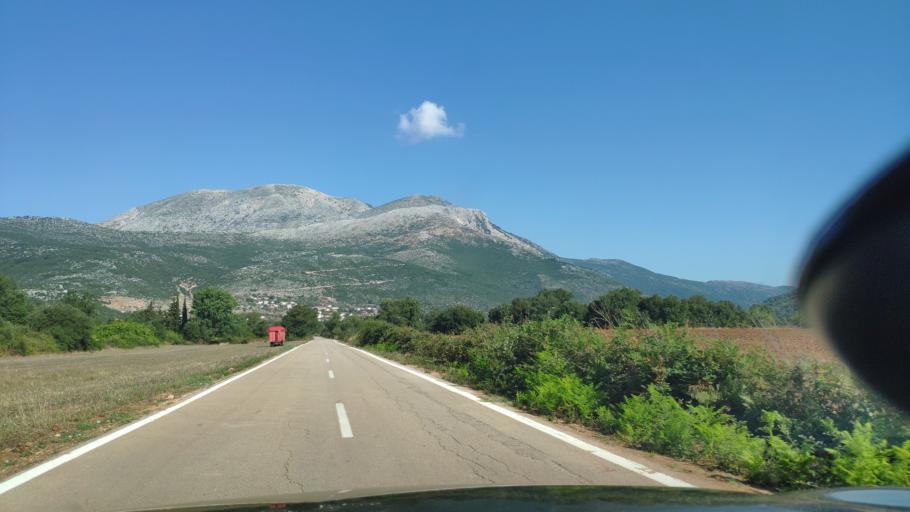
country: GR
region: West Greece
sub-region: Nomos Aitolias kai Akarnanias
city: Archontochorion
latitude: 38.6979
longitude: 21.0992
